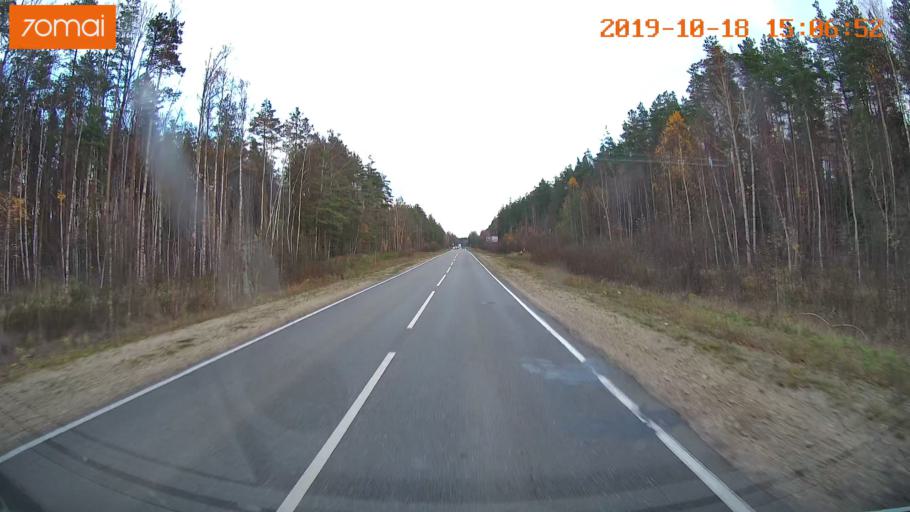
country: RU
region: Vladimir
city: Gus'-Khrustal'nyy
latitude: 55.5349
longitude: 40.5850
